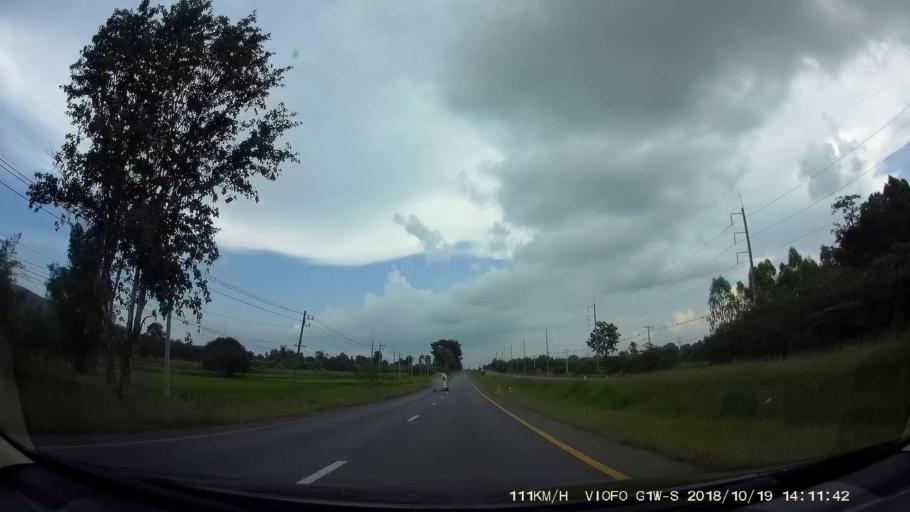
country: TH
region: Chaiyaphum
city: Khon Sawan
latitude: 15.9413
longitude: 102.1637
